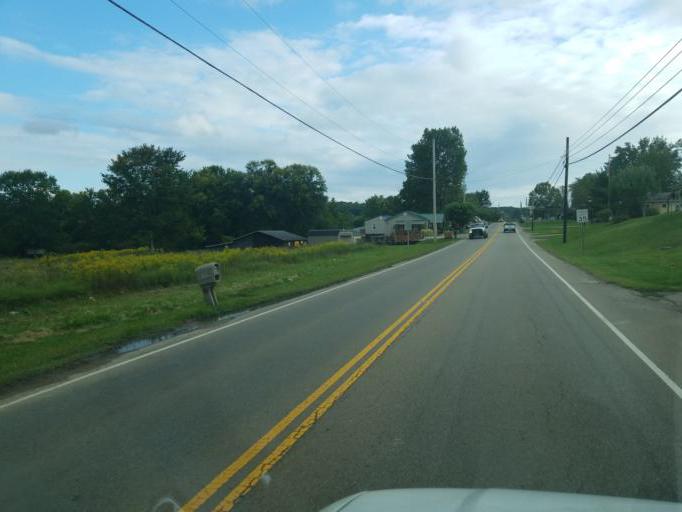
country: US
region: Ohio
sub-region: Jackson County
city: Oak Hill
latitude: 38.9045
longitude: -82.5688
